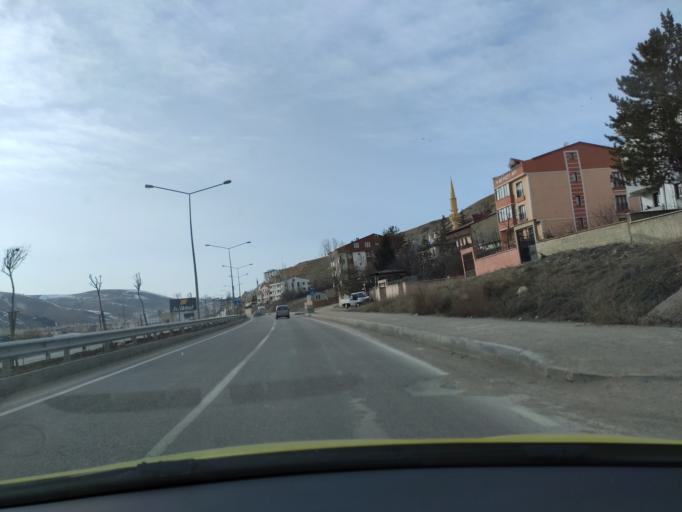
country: TR
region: Bayburt
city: Bayburt
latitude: 40.2426
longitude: 40.2438
